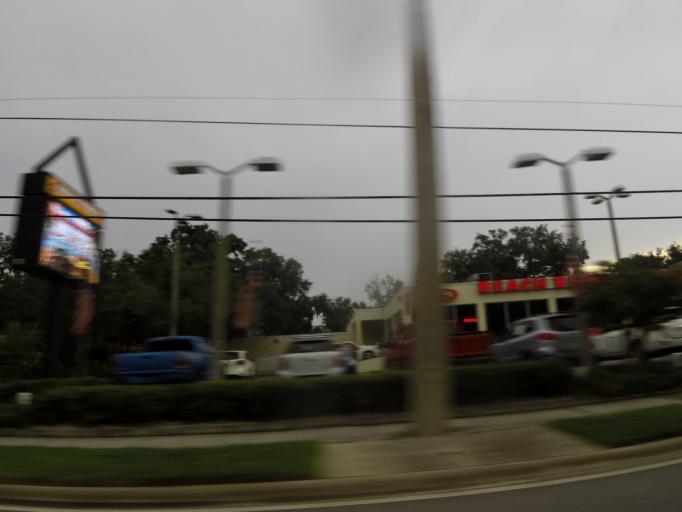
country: US
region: Florida
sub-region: Duval County
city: Jacksonville
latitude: 30.2874
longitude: -81.5873
